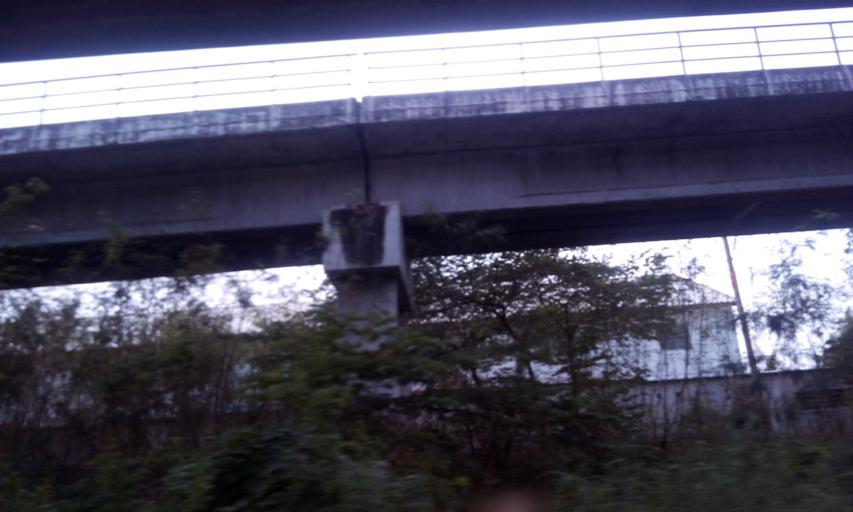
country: TH
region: Chachoengsao
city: Chachoengsao
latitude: 13.6980
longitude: 101.0873
